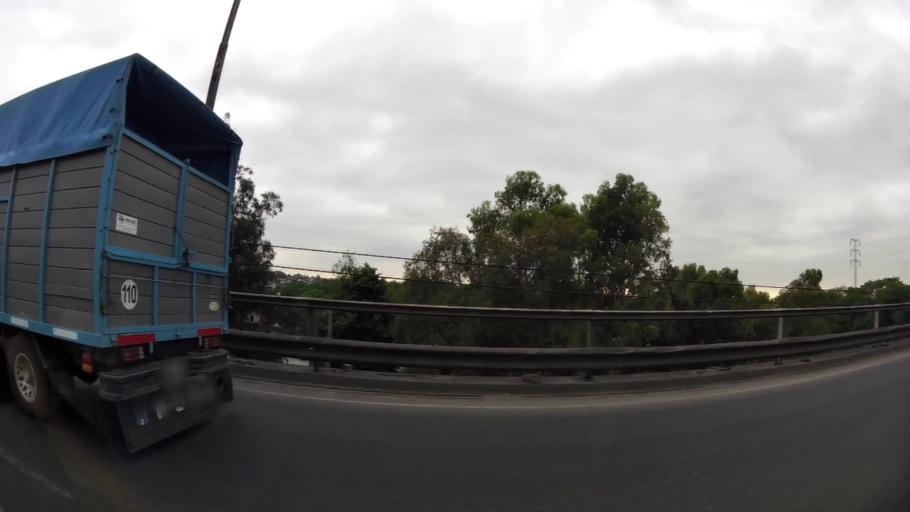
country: AR
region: Buenos Aires
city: San Justo
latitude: -34.7161
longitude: -58.5202
